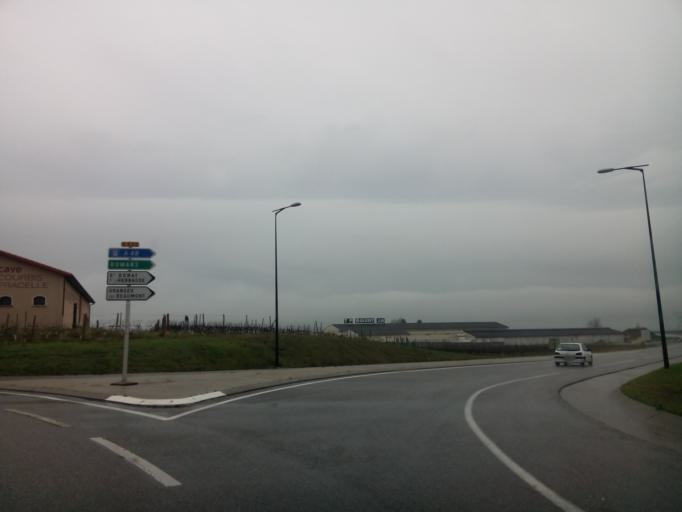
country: FR
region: Rhone-Alpes
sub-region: Departement de la Drome
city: Chanos-Curson
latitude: 45.0601
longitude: 4.9061
